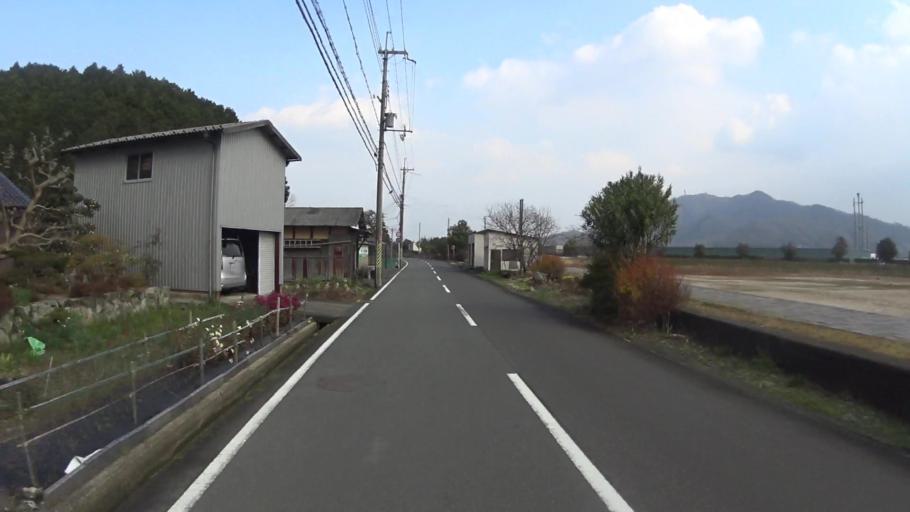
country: JP
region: Kyoto
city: Maizuru
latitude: 35.4606
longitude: 135.3138
